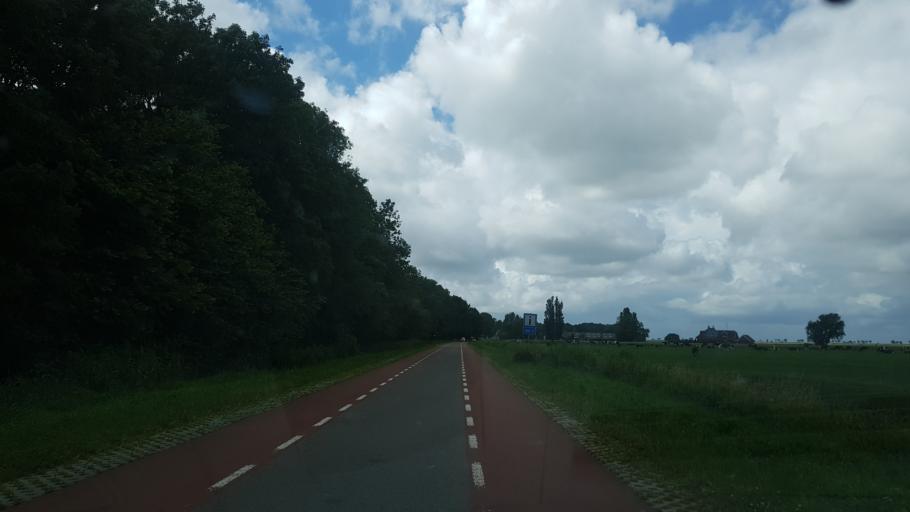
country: NL
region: Groningen
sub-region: Gemeente Winsum
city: Winsum
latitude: 53.3974
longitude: 6.4932
